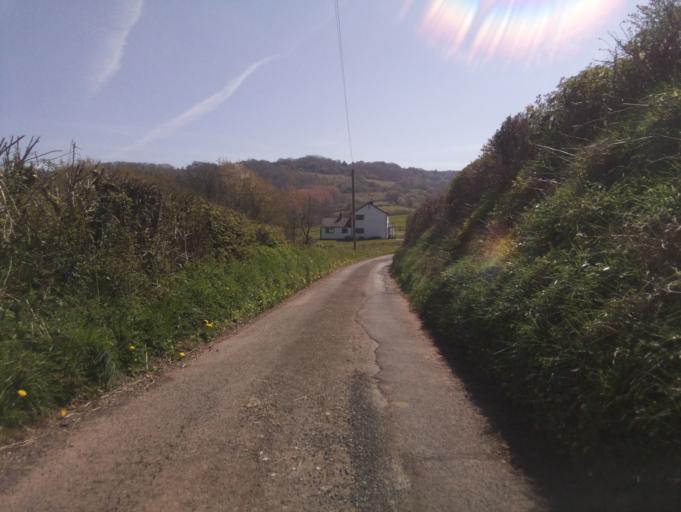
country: GB
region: Wales
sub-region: Monmouthshire
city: Llangwm
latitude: 51.6927
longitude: -2.8256
